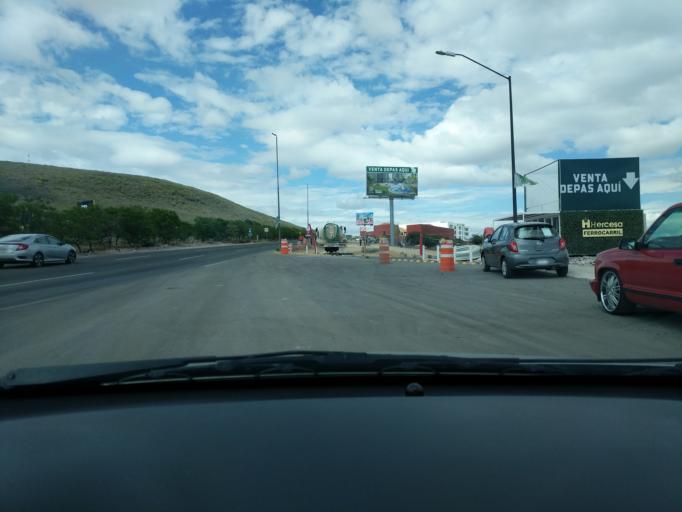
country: MX
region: Queretaro
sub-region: El Marques
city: La Pradera
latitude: 20.6595
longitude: -100.3529
